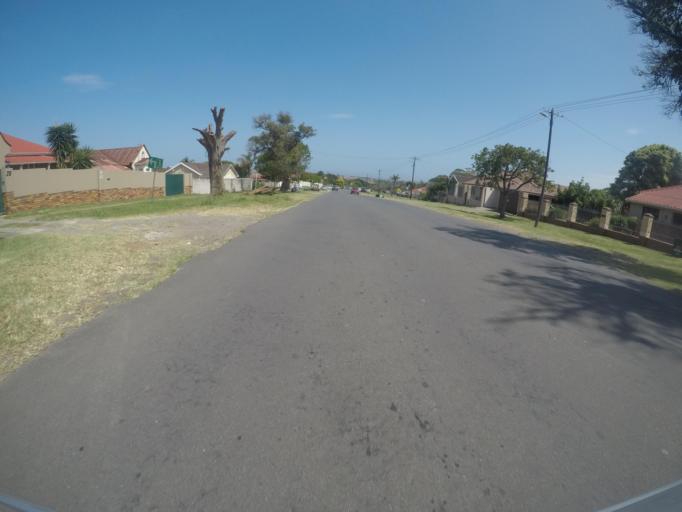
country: ZA
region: Eastern Cape
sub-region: Buffalo City Metropolitan Municipality
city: East London
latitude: -32.9798
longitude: 27.8855
